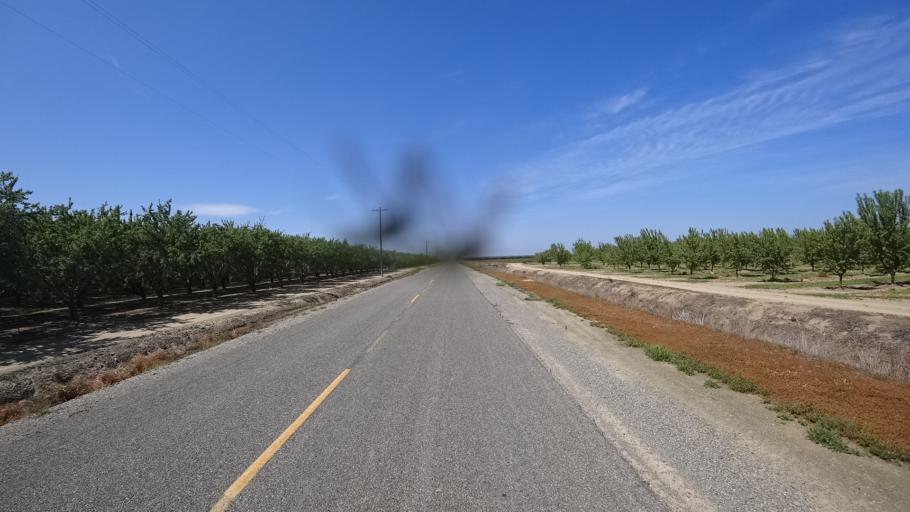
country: US
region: California
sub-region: Glenn County
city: Hamilton City
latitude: 39.6524
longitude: -122.0698
